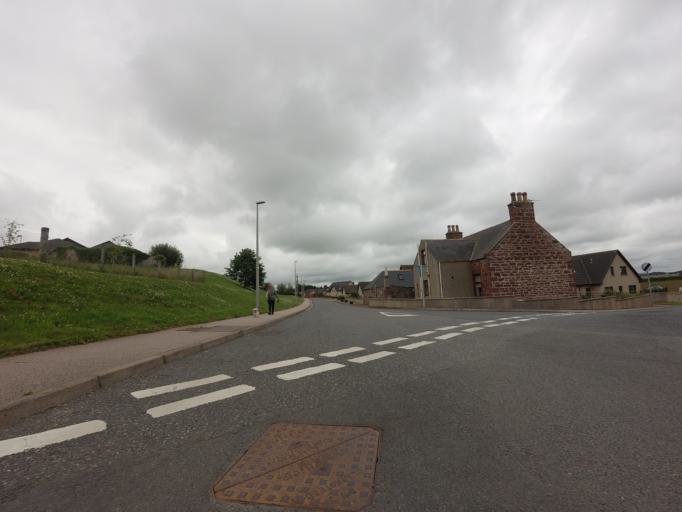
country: GB
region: Scotland
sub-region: Aberdeenshire
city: Turriff
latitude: 57.5358
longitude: -2.4441
